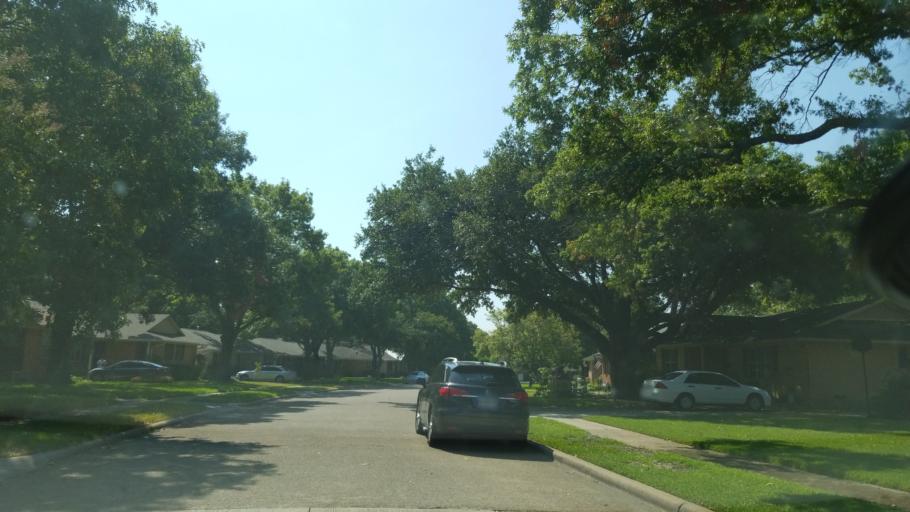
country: US
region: Texas
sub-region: Dallas County
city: Garland
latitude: 32.8774
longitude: -96.7048
